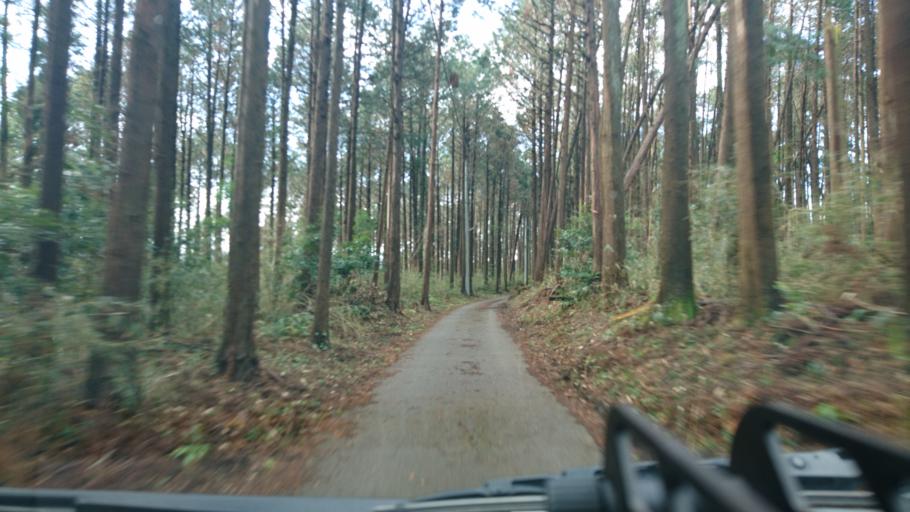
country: JP
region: Chiba
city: Kimitsu
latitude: 35.2895
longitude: 139.9661
